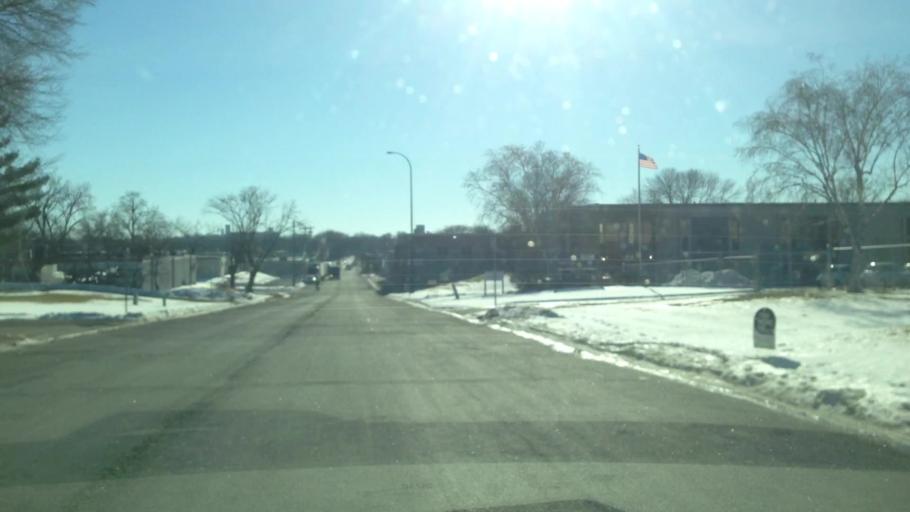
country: US
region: Minnesota
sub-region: Ramsey County
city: Lauderdale
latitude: 44.9965
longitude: -93.2178
